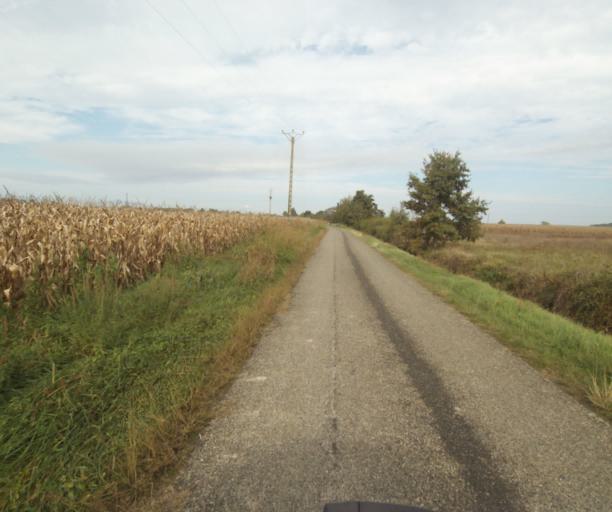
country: FR
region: Midi-Pyrenees
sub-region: Departement du Tarn-et-Garonne
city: Finhan
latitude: 43.9157
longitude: 1.2369
